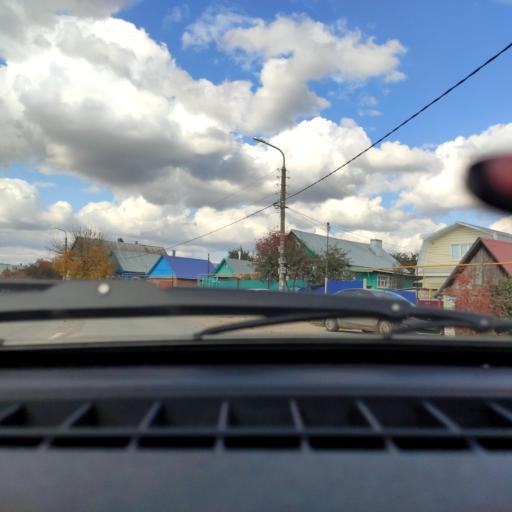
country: RU
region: Bashkortostan
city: Ufa
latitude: 54.7388
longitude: 55.9216
